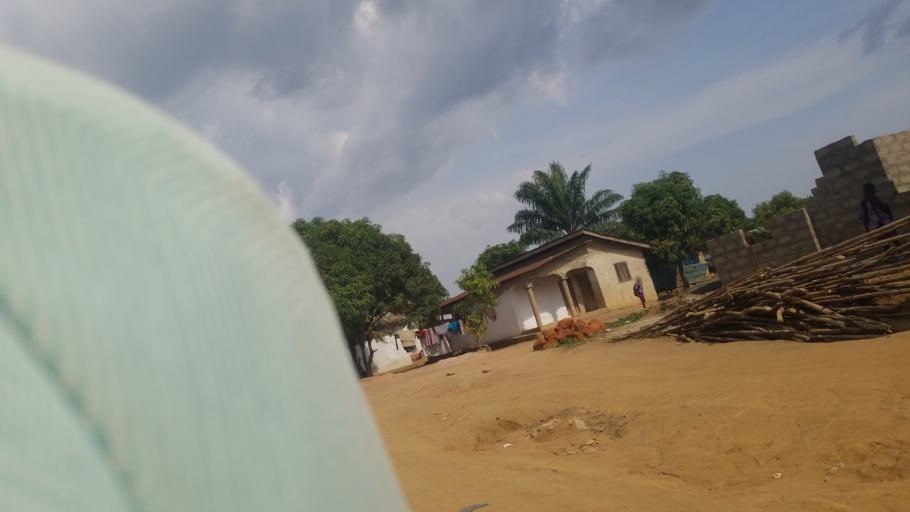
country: SL
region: Western Area
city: Waterloo
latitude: 8.3161
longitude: -13.0482
